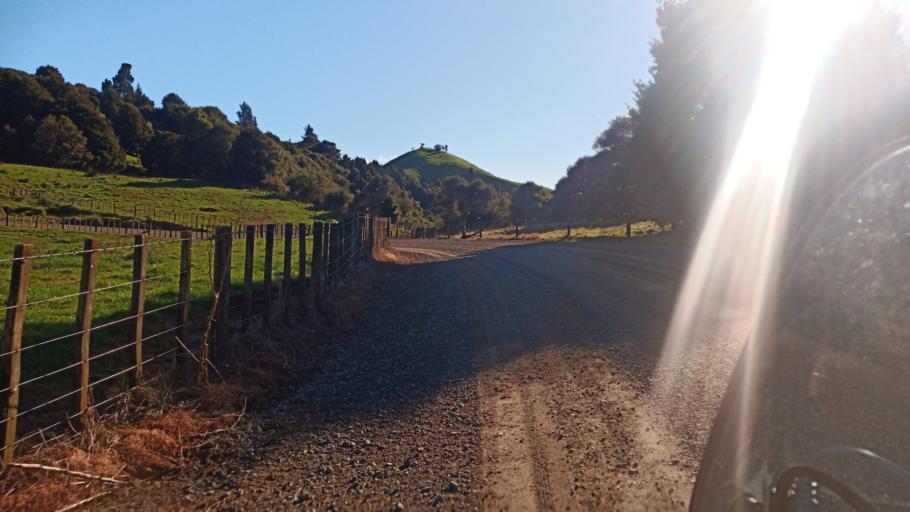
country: NZ
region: Hawke's Bay
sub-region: Wairoa District
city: Wairoa
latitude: -38.8118
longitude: 177.2908
